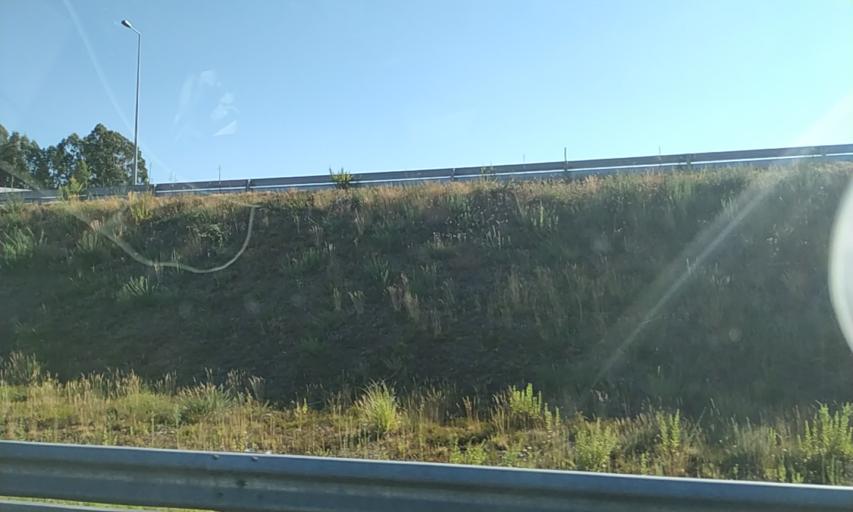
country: PT
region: Porto
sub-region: Valongo
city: Sobrado
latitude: 41.2291
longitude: -8.4546
